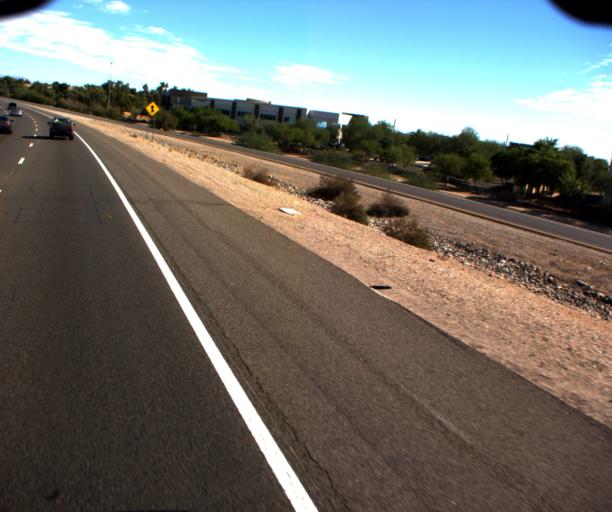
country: US
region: Arizona
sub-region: Maricopa County
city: Peoria
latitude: 33.6116
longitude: -112.2420
